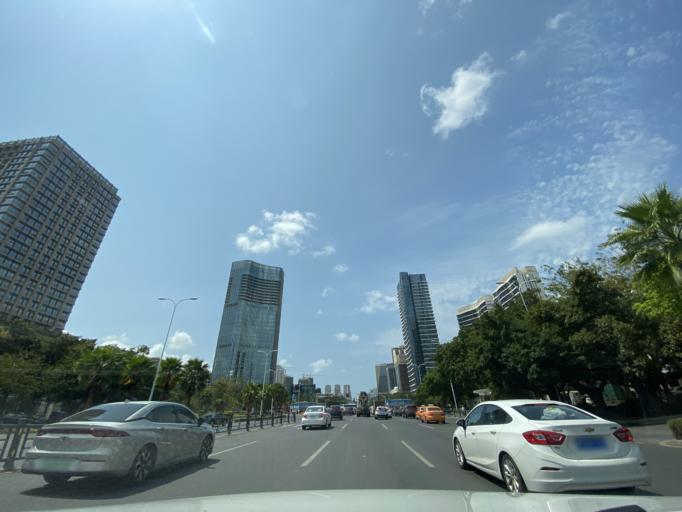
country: CN
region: Hainan
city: Sanya
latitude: 18.2781
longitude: 109.5101
